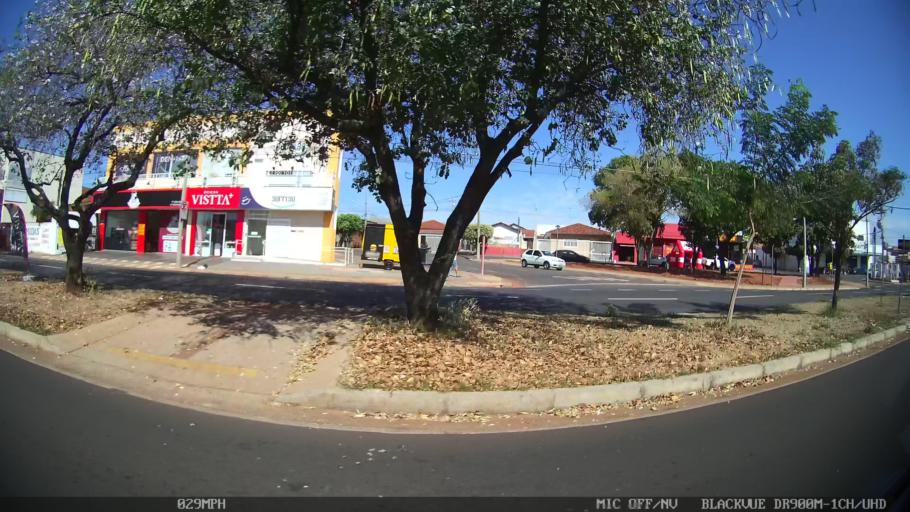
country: BR
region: Sao Paulo
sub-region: Sao Jose Do Rio Preto
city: Sao Jose do Rio Preto
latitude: -20.7814
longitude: -49.3991
